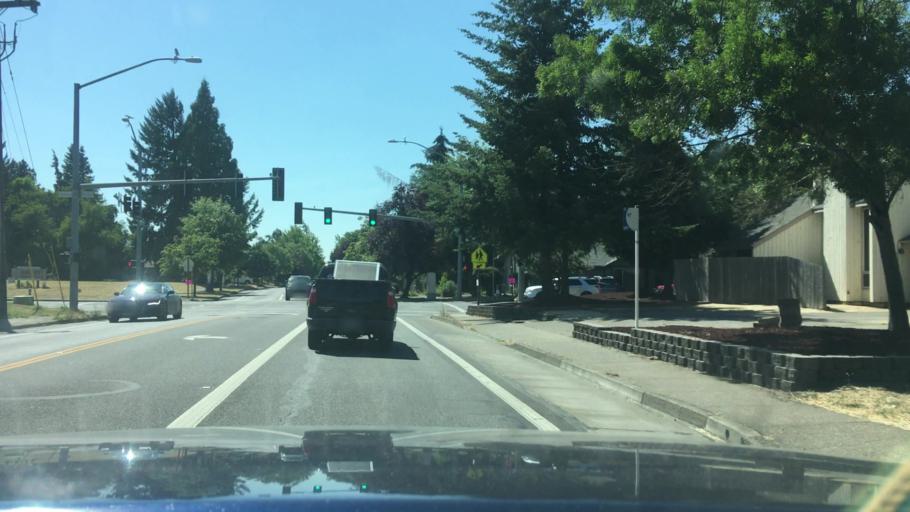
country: US
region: Oregon
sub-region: Lane County
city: Eugene
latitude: 44.0930
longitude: -123.0803
